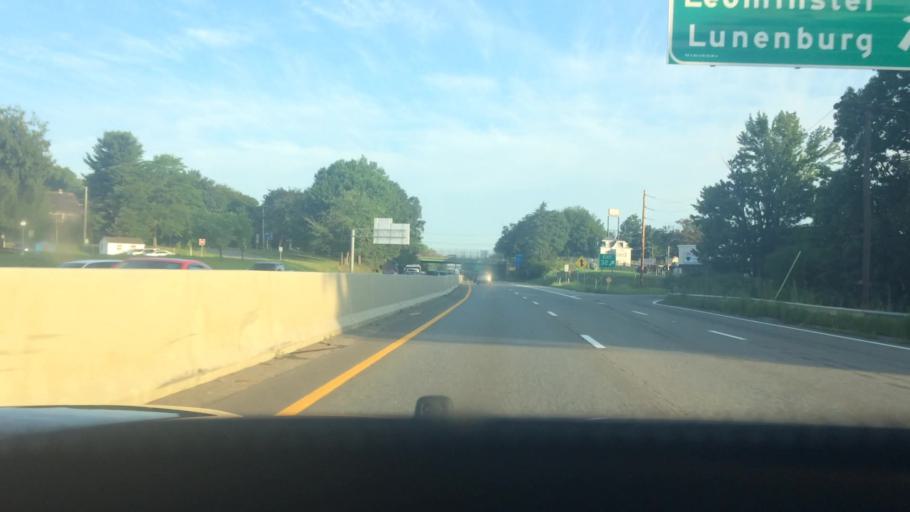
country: US
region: Massachusetts
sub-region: Worcester County
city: Leominster
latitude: 42.5358
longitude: -71.7415
